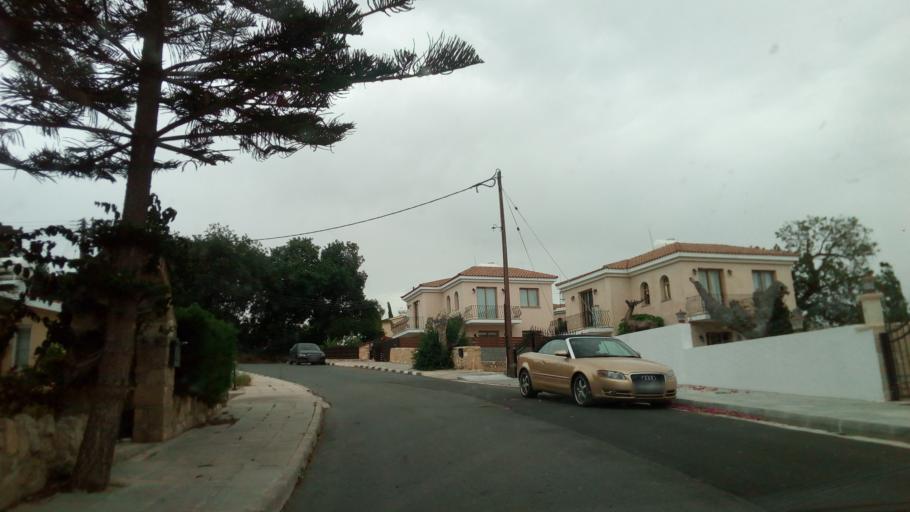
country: CY
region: Pafos
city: Mesogi
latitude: 34.8135
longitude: 32.4429
